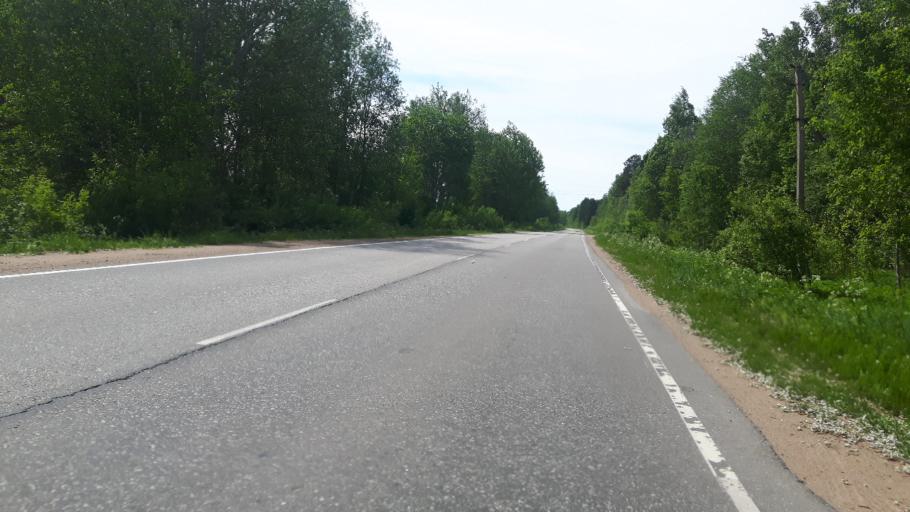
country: RU
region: Leningrad
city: Ust'-Luga
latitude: 59.6504
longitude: 28.2356
